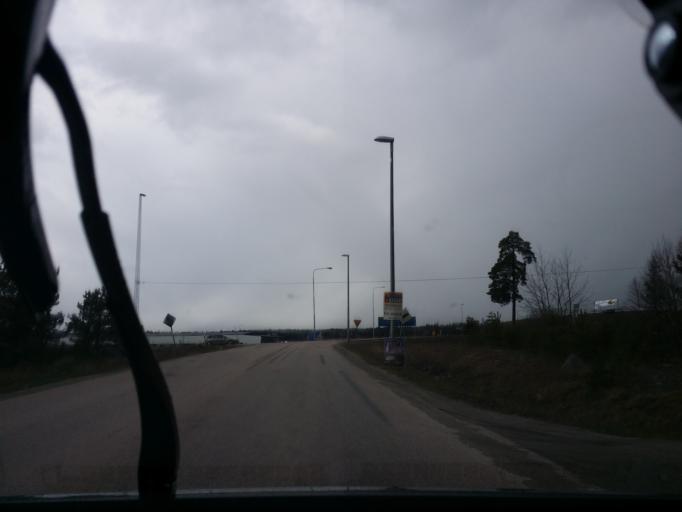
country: SE
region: Uppsala
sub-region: Enkopings Kommun
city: Enkoping
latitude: 59.6456
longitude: 17.1422
